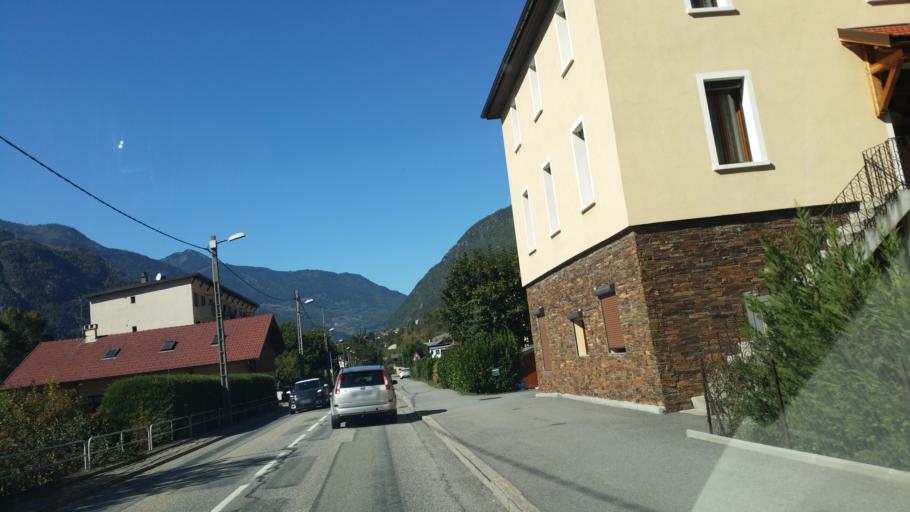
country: FR
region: Rhone-Alpes
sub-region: Departement de la Savoie
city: Aigueblanche
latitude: 45.5049
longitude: 6.5055
